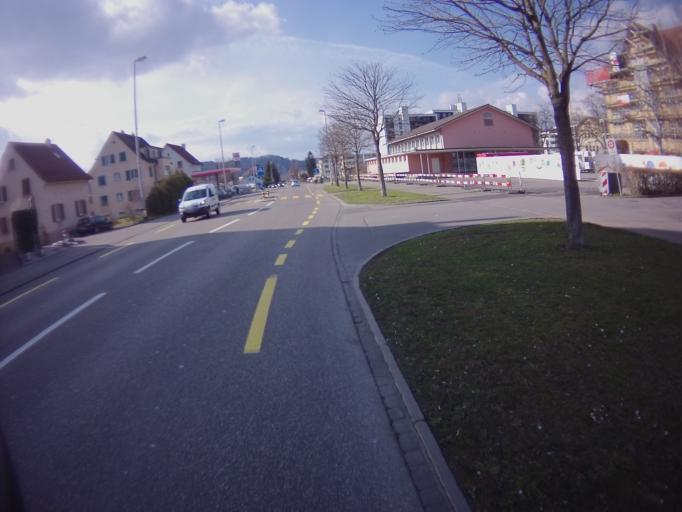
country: CH
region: Aargau
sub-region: Bezirk Baden
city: Neuenhof
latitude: 47.4510
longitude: 8.3255
